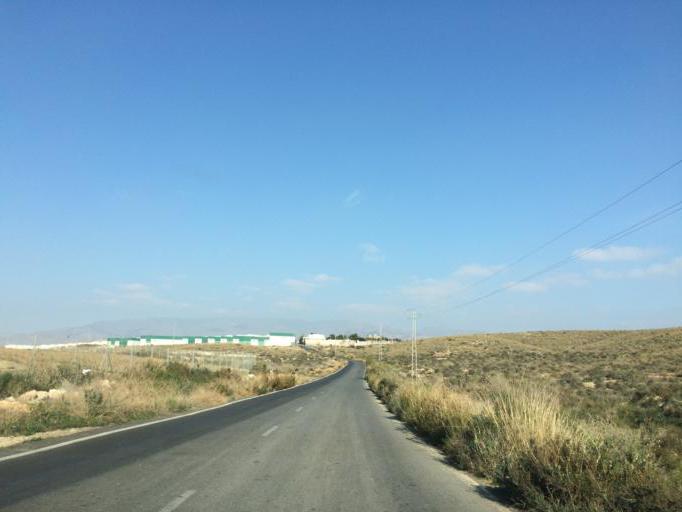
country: ES
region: Andalusia
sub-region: Provincia de Almeria
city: Viator
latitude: 36.8698
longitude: -2.4184
